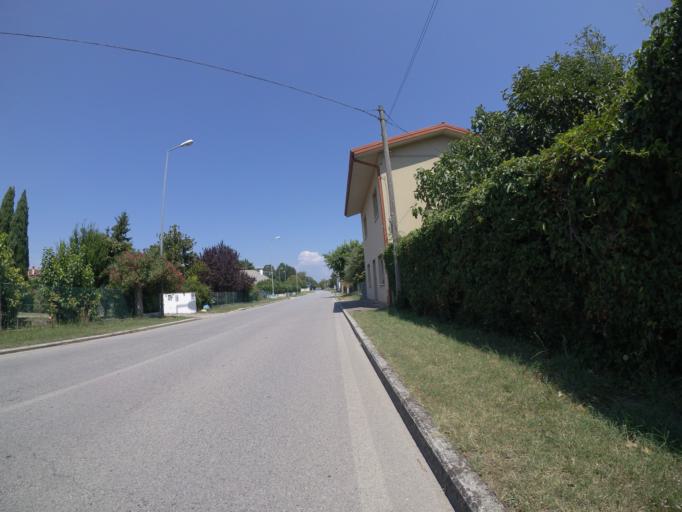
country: IT
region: Friuli Venezia Giulia
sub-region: Provincia di Udine
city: Mortegliano
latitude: 45.9403
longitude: 13.1661
